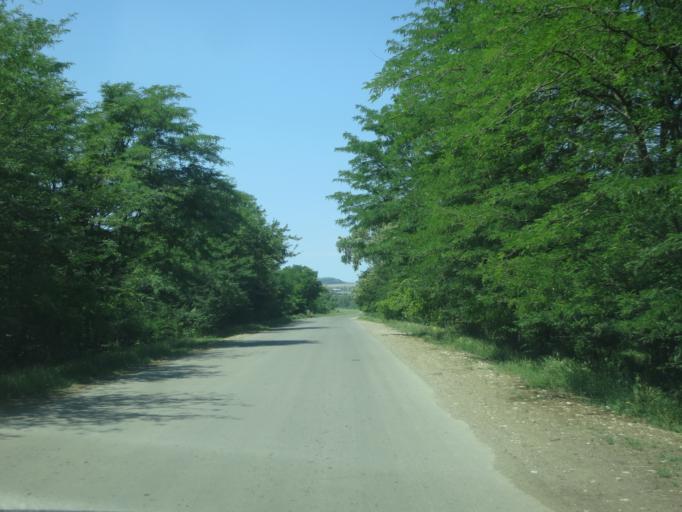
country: GE
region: Kakheti
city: Sagarejo
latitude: 41.6671
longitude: 45.3870
